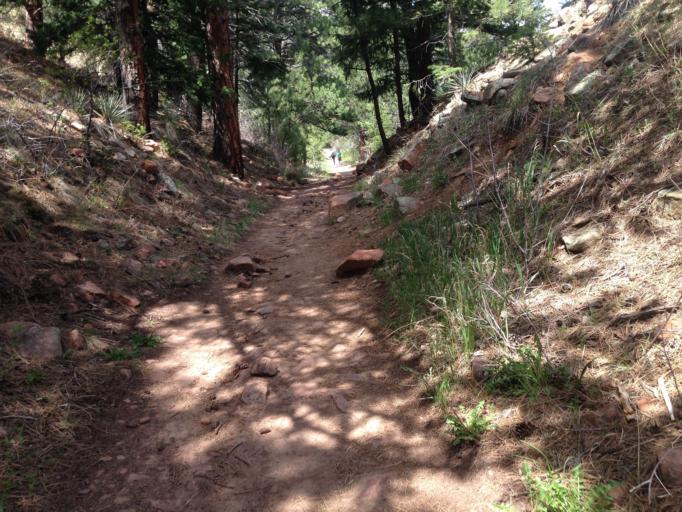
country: US
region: Colorado
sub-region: Boulder County
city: Boulder
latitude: 39.9289
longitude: -105.2798
